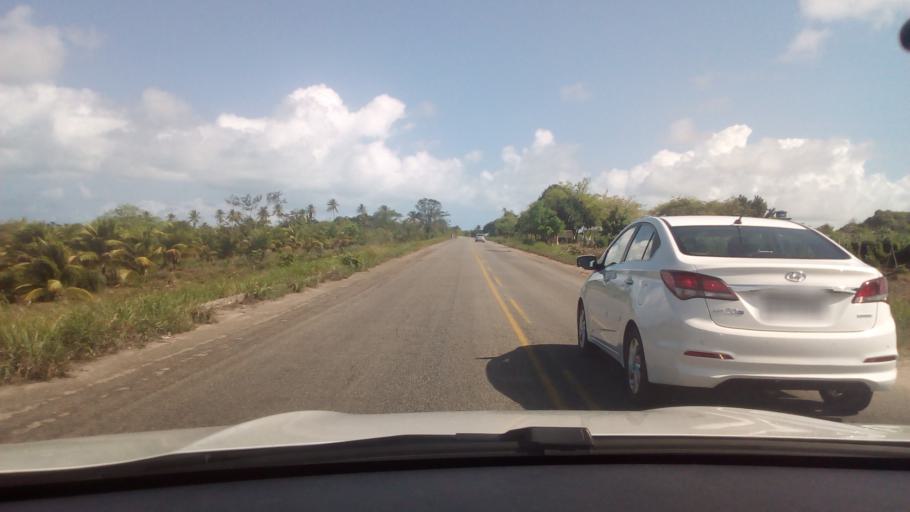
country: BR
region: Paraiba
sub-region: Conde
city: Conde
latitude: -7.2436
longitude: -34.8321
